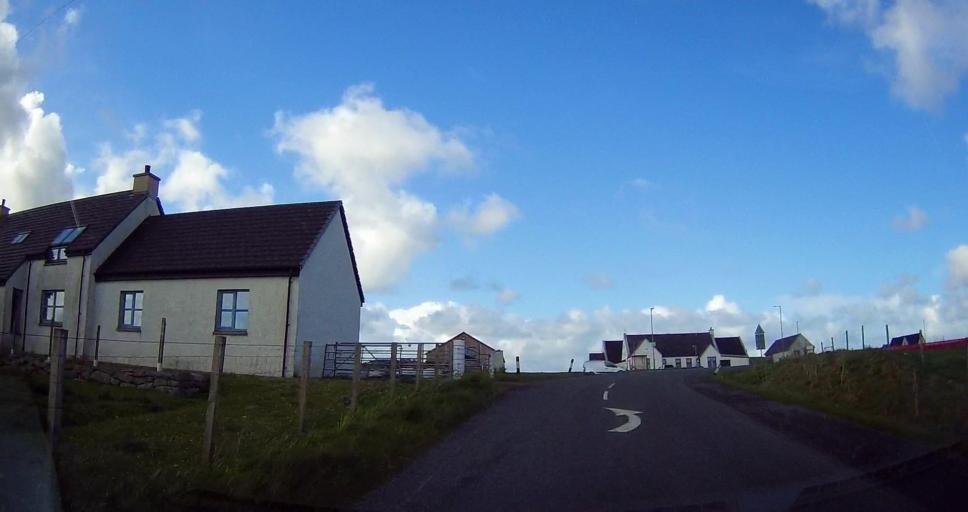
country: GB
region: Scotland
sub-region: Shetland Islands
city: Shetland
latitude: 60.3683
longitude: -1.1407
